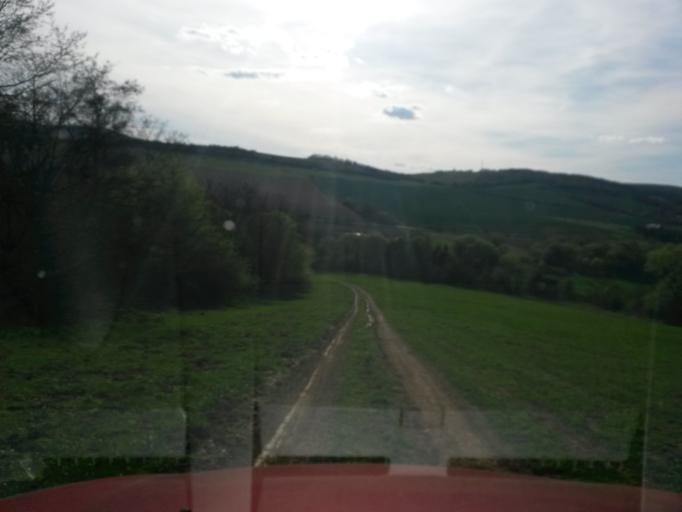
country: SK
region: Presovsky
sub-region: Okres Presov
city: Presov
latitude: 48.9209
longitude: 21.2023
